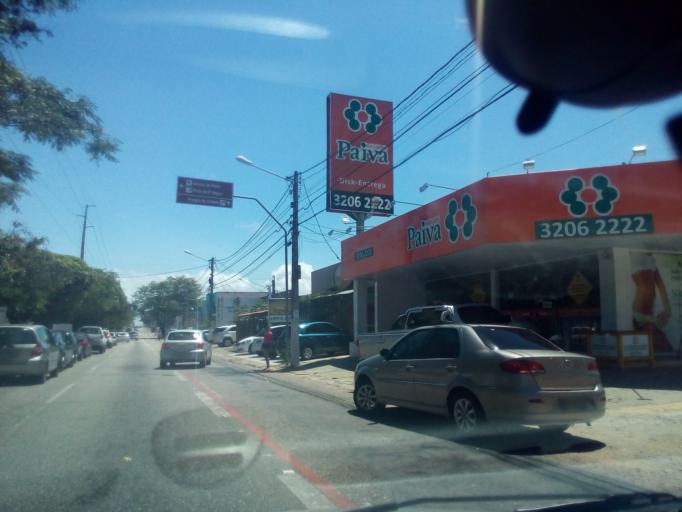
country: BR
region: Rio Grande do Norte
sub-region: Natal
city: Natal
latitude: -5.8364
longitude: -35.2193
